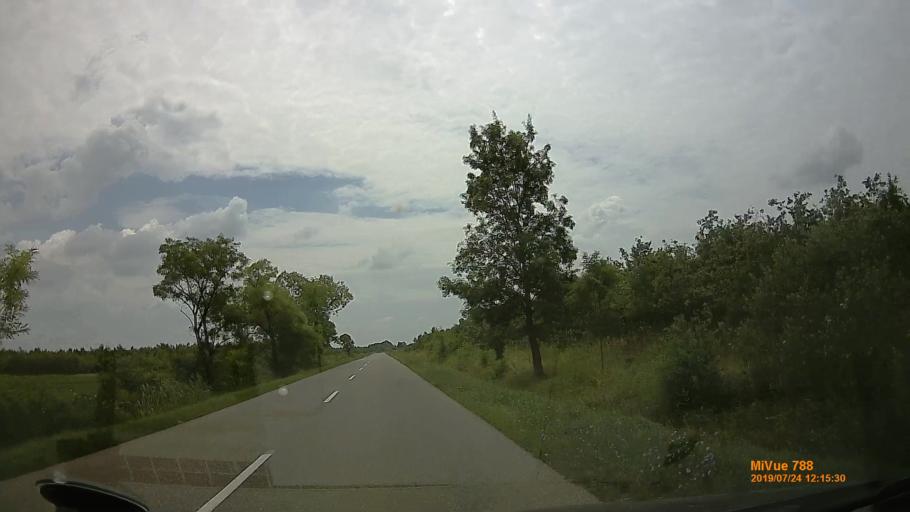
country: HU
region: Szabolcs-Szatmar-Bereg
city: Vasarosnameny
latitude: 48.1835
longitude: 22.3453
